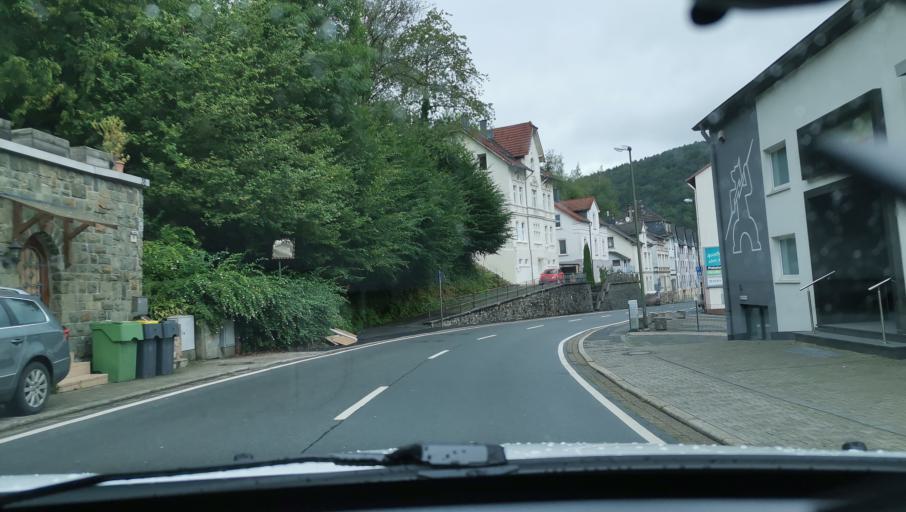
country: DE
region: North Rhine-Westphalia
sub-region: Regierungsbezirk Arnsberg
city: Schalksmuhle
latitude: 51.2382
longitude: 7.5286
